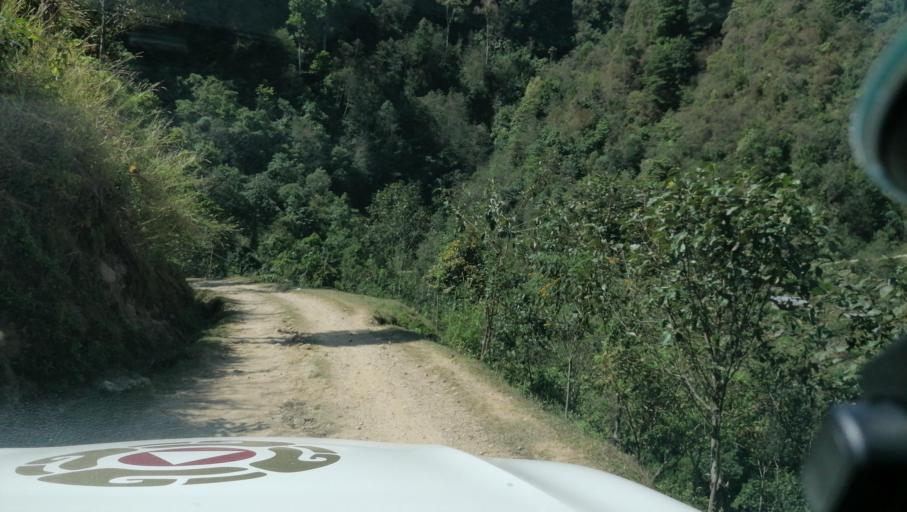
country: GT
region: San Marcos
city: Tacana
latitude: 15.2072
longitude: -92.2109
